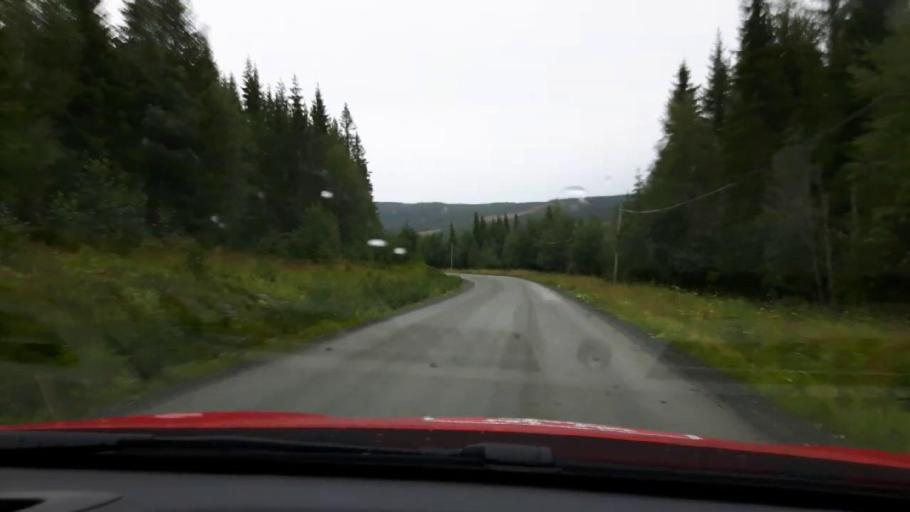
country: SE
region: Jaemtland
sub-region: Are Kommun
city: Are
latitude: 63.4014
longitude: 12.8408
